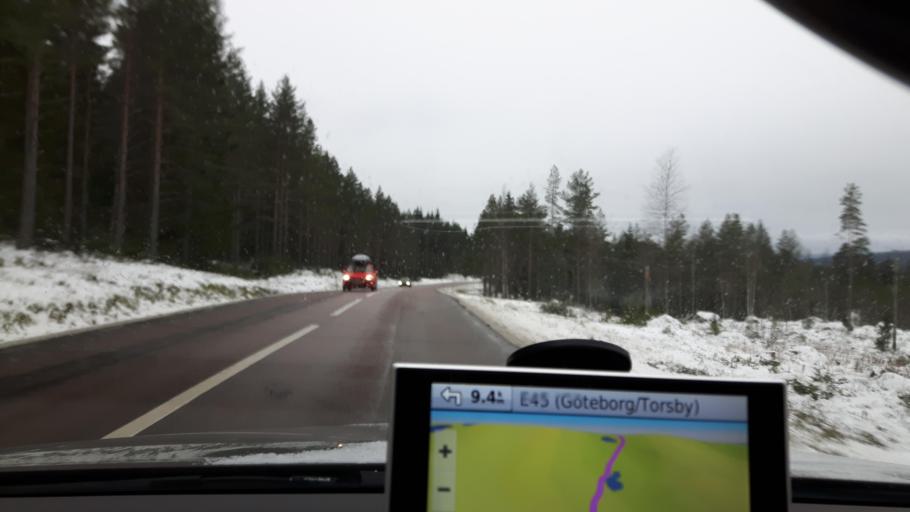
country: SE
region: Vaermland
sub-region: Torsby Kommun
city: Torsby
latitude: 60.3402
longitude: 13.1504
